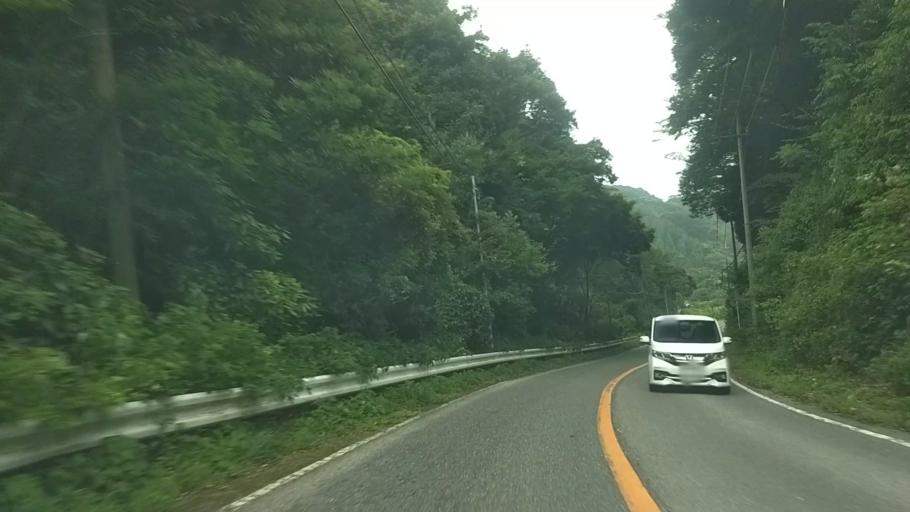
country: JP
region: Chiba
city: Tateyama
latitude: 35.1397
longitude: 139.9069
